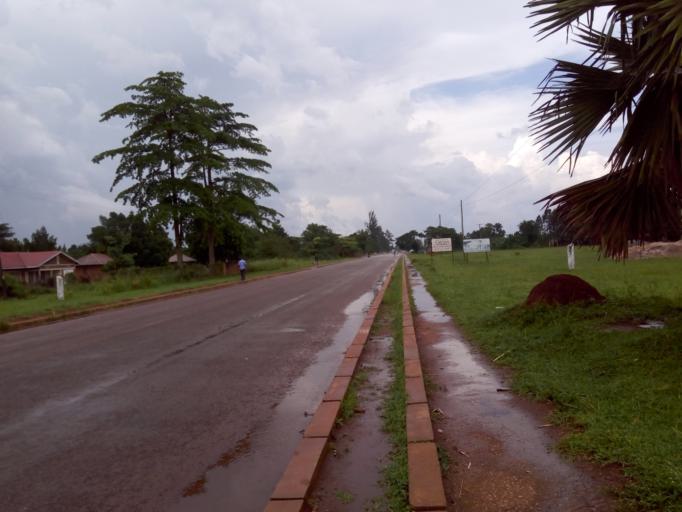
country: UG
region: Western Region
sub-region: Masindi District
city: Masindi
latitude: 1.6867
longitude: 31.7057
